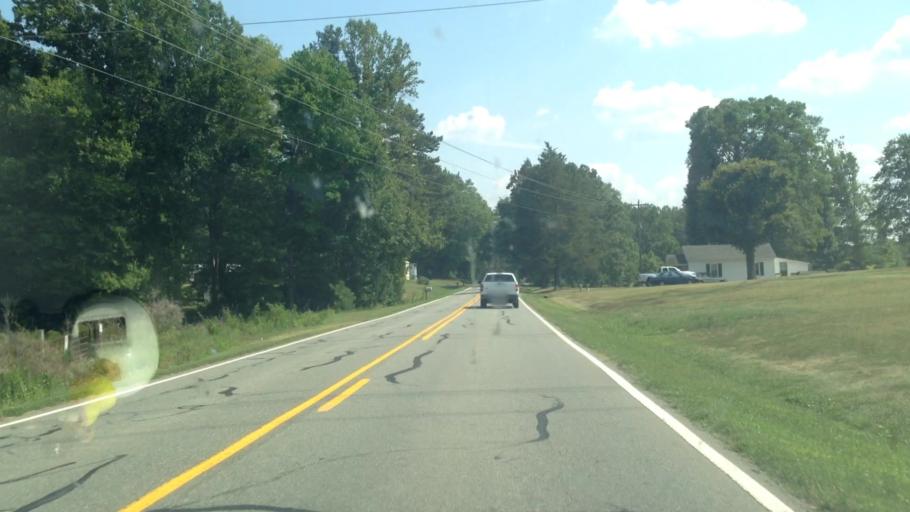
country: US
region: North Carolina
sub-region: Stokes County
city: Walnut Cove
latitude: 36.2739
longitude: -80.0883
